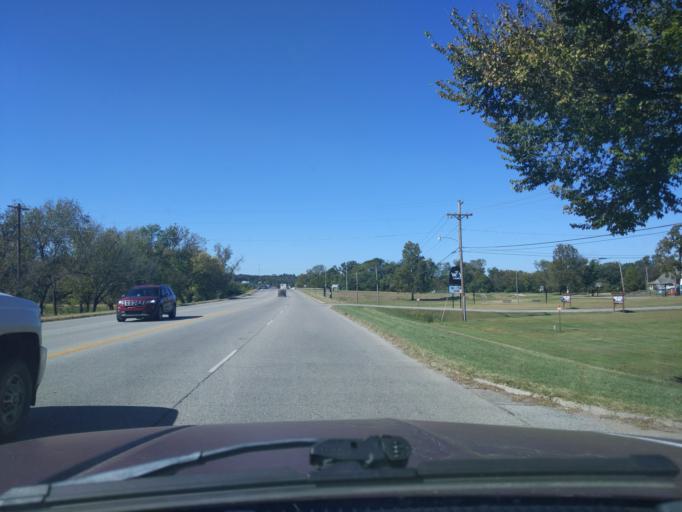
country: US
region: Oklahoma
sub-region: Creek County
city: Sapulpa
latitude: 35.9885
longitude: -96.1240
